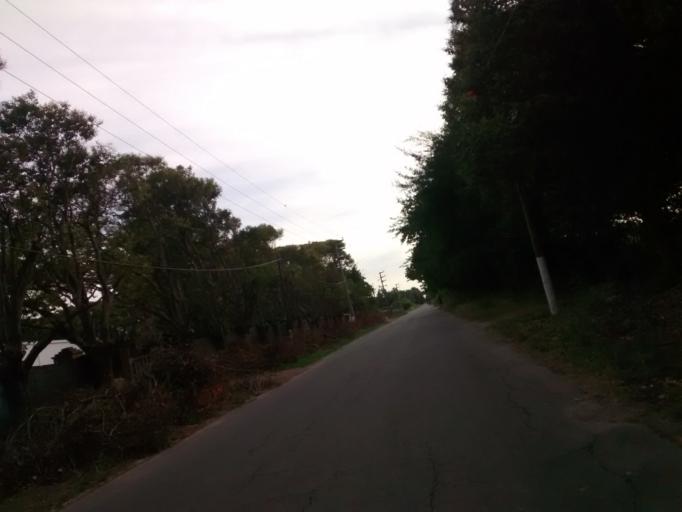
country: AR
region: Buenos Aires
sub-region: Partido de La Plata
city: La Plata
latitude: -34.8426
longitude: -58.0931
